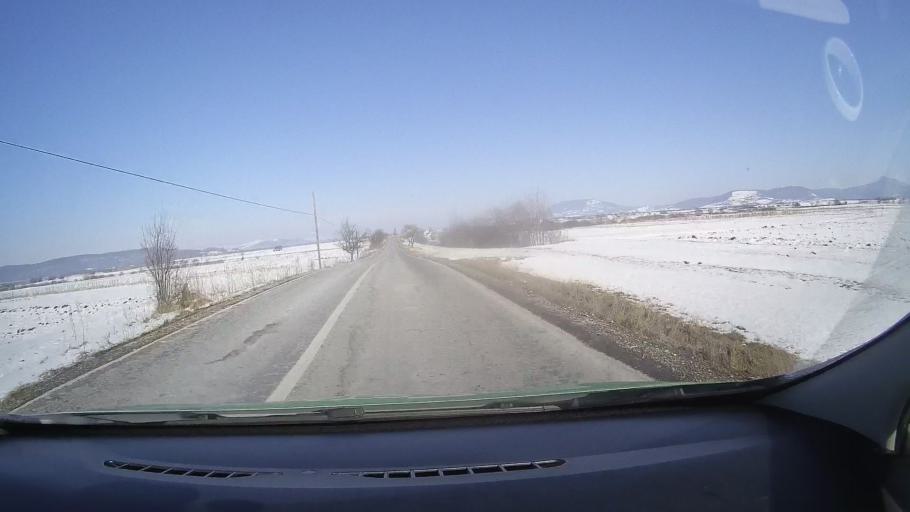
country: RO
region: Brasov
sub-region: Comuna Parau
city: Parau
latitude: 45.8514
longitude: 25.1932
